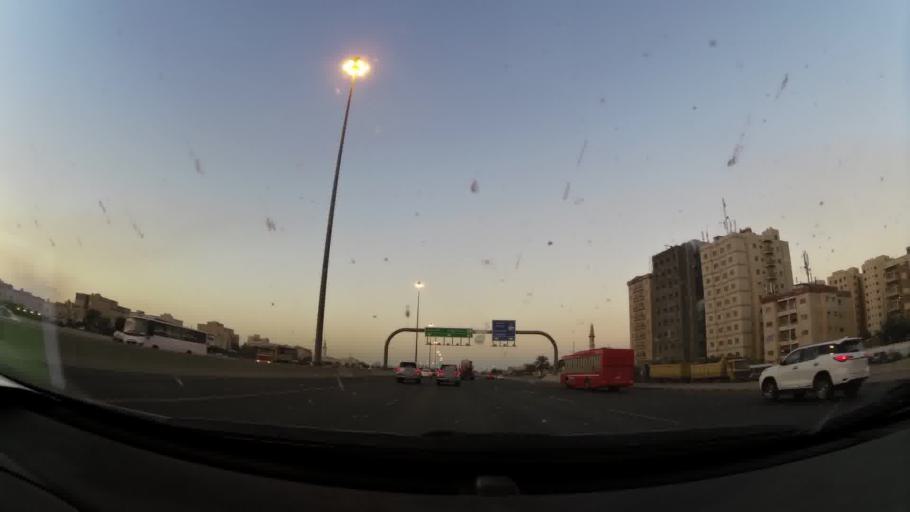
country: KW
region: Al Ahmadi
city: Al Manqaf
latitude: 29.0997
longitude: 48.1176
